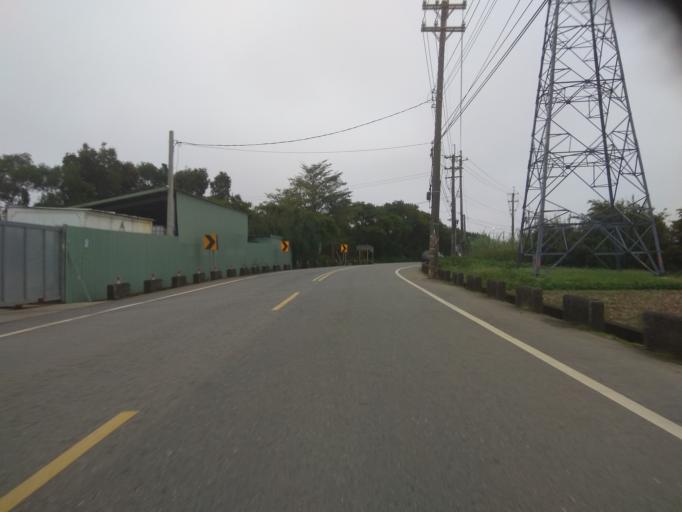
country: TW
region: Taiwan
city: Taoyuan City
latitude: 24.9890
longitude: 121.1239
